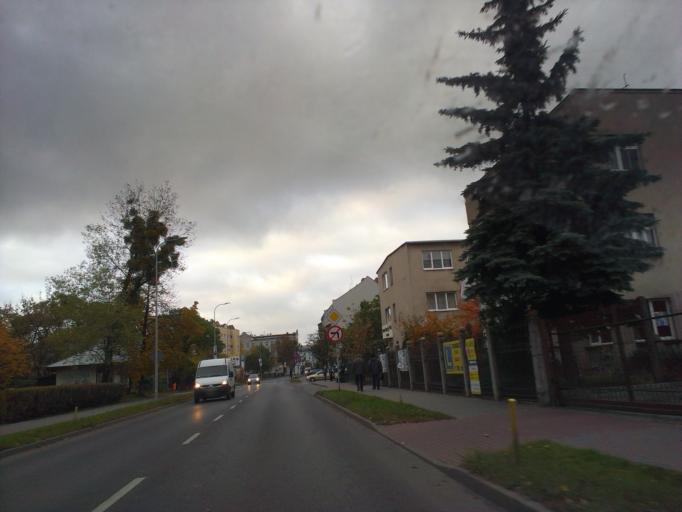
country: PL
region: Kujawsko-Pomorskie
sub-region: Torun
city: Torun
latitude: 53.0193
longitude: 18.6027
